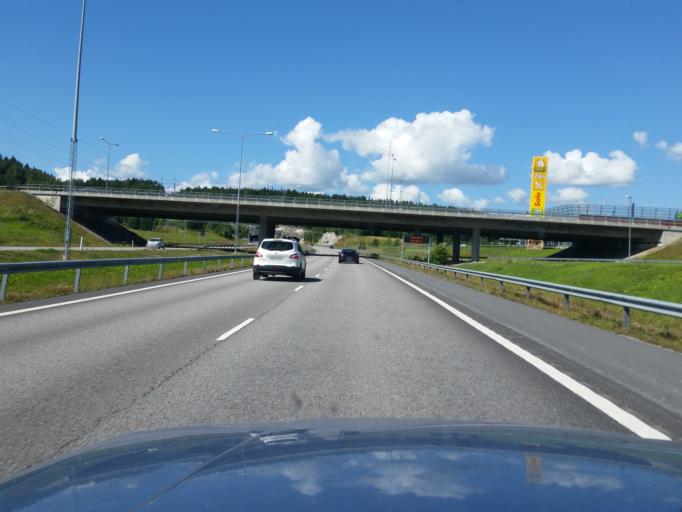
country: FI
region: Varsinais-Suomi
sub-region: Salo
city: Salo
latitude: 60.4174
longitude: 23.1675
